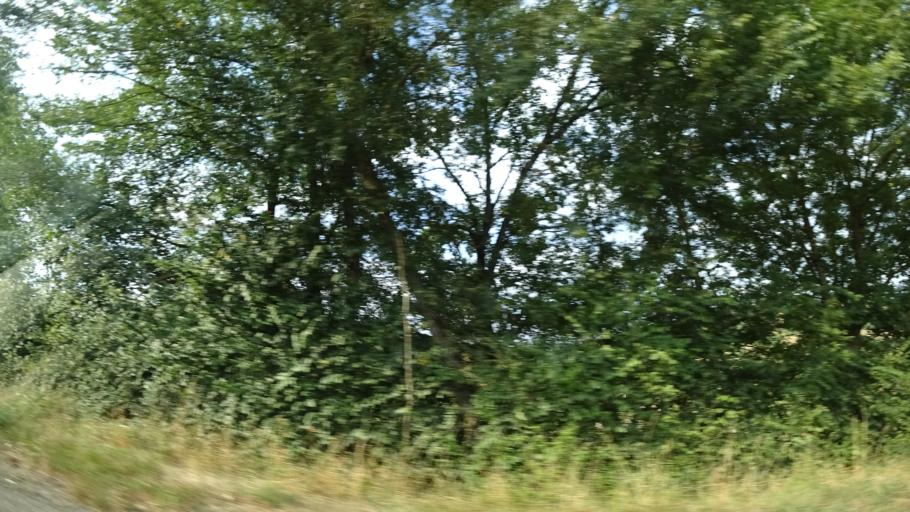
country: FR
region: Midi-Pyrenees
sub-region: Departement de l'Aveyron
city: Saint-Christophe-Vallon
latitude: 44.4958
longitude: 2.3854
